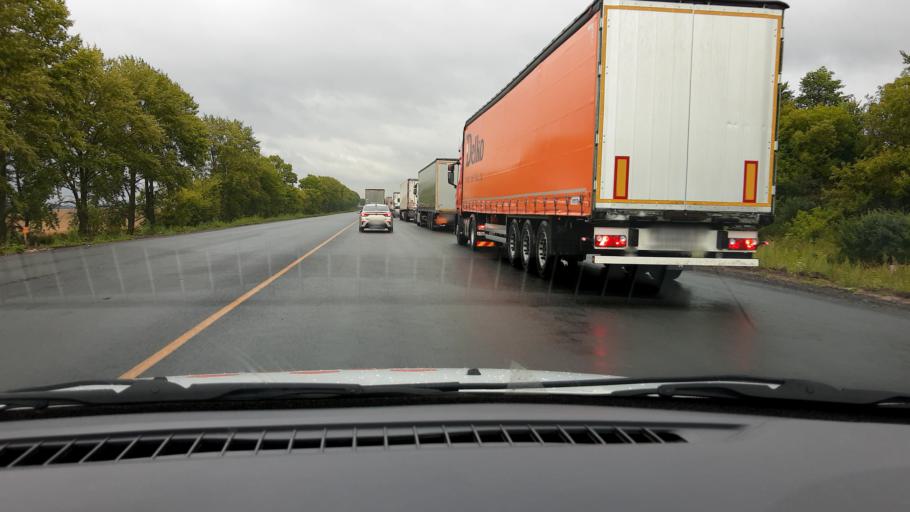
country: RU
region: Chuvashia
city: Yantikovo
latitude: 55.8013
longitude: 47.8785
